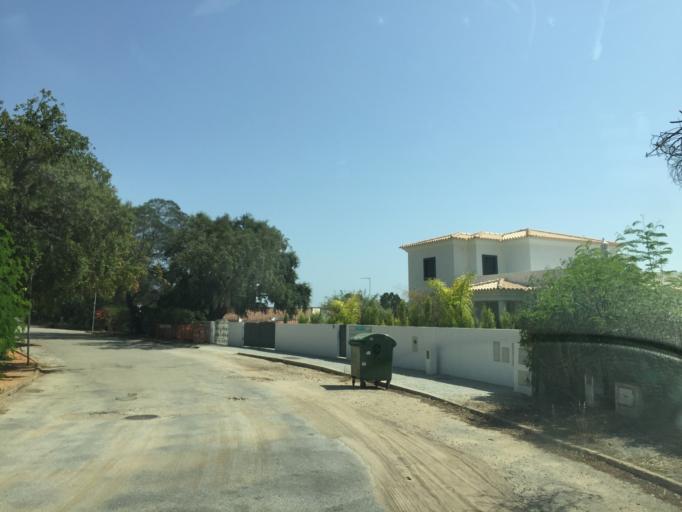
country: PT
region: Faro
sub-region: Albufeira
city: Ferreiras
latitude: 37.1063
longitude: -8.2047
